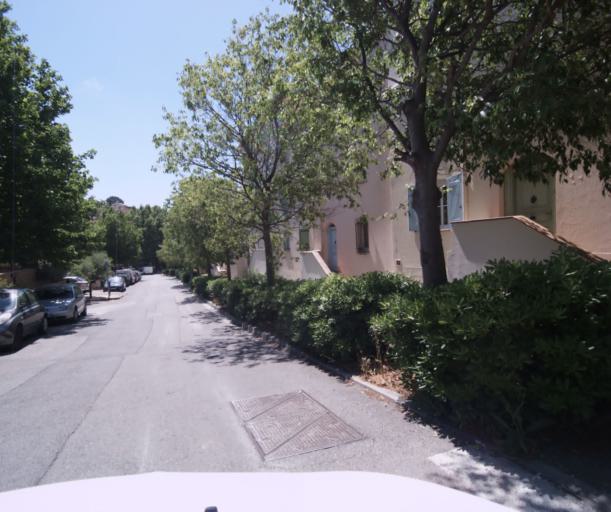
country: FR
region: Provence-Alpes-Cote d'Azur
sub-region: Departement du Var
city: Le Revest-les-Eaux
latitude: 43.1776
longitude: 5.9246
